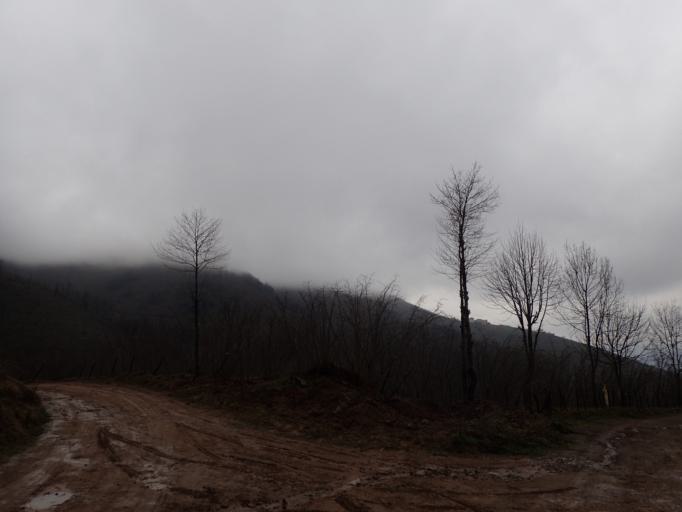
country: TR
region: Ordu
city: Camas
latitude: 40.8611
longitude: 37.5169
